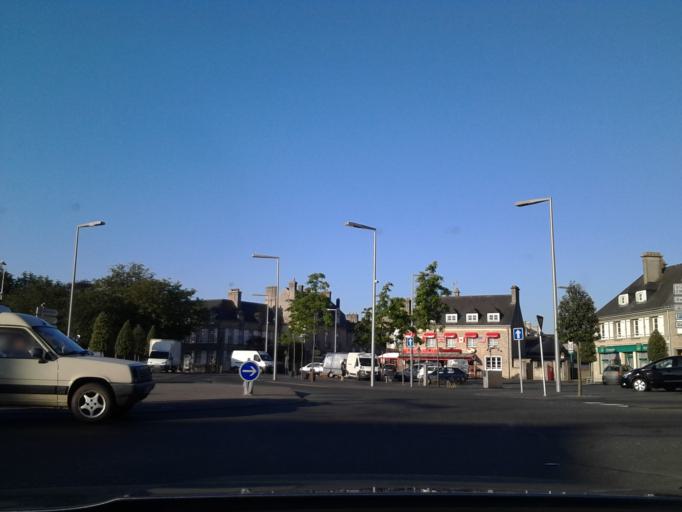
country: FR
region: Lower Normandy
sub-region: Departement de la Manche
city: Valognes
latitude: 49.5095
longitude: -1.4719
